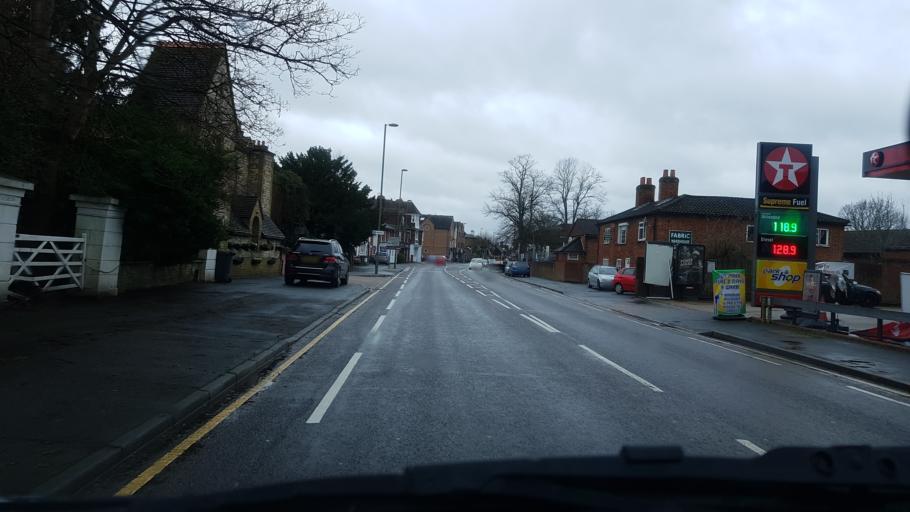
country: GB
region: England
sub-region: Surrey
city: Godalming
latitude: 51.1940
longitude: -0.5972
